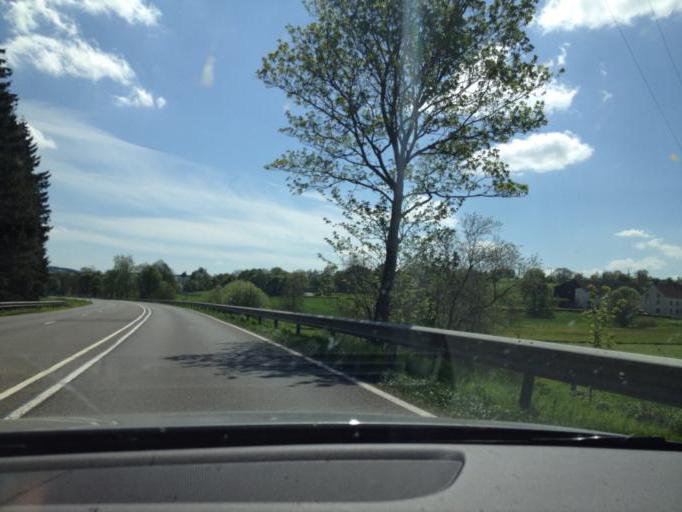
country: DE
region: Rheinland-Pfalz
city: Neuendorf
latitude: 50.2808
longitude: 6.4606
